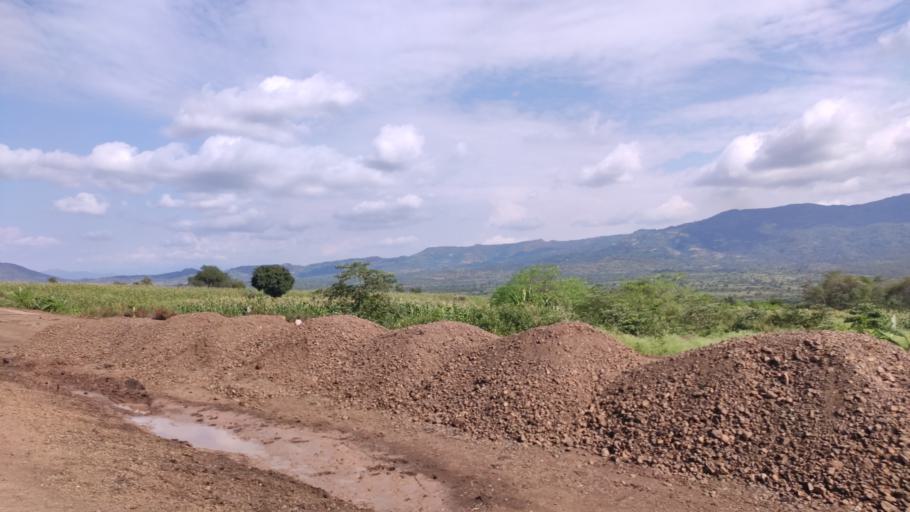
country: ET
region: Southern Nations, Nationalities, and People's Region
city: Felege Neway
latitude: 6.3974
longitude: 37.1121
